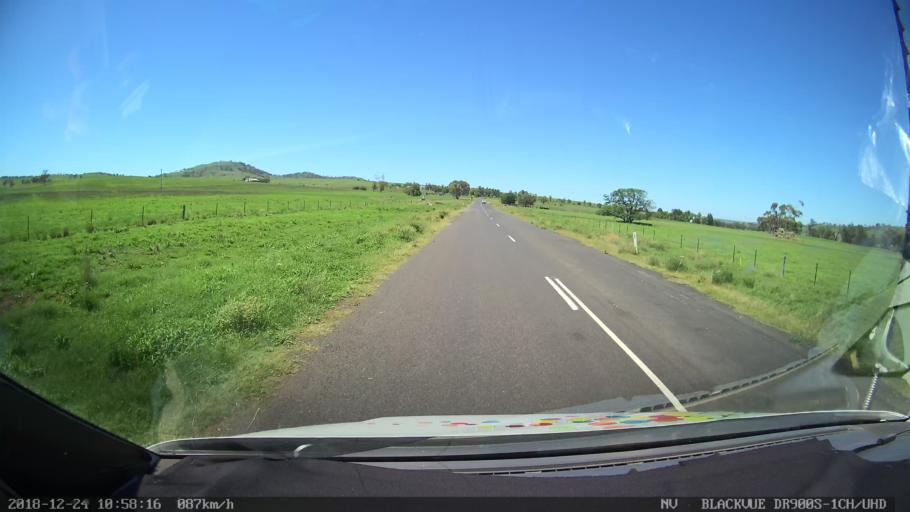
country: AU
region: New South Wales
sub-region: Upper Hunter Shire
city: Merriwa
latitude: -32.0453
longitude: 150.4070
